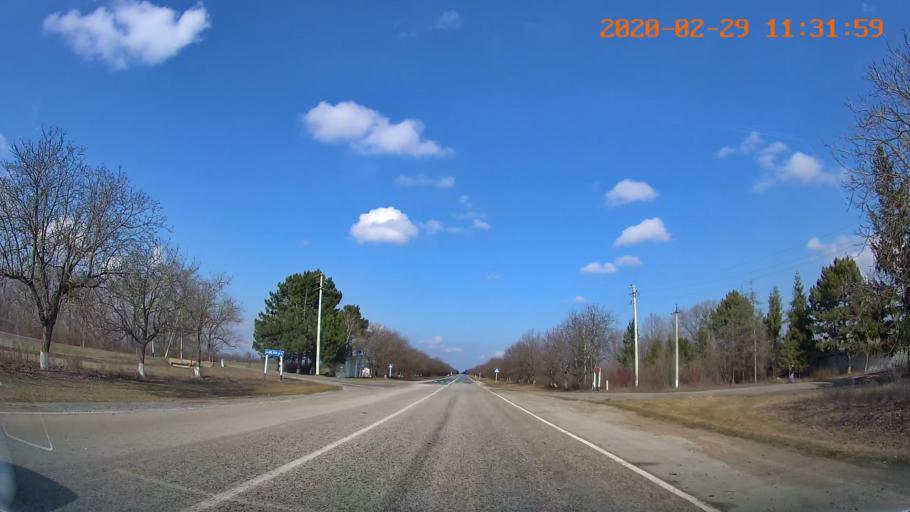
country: MD
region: Rezina
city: Saharna
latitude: 47.5314
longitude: 29.0992
